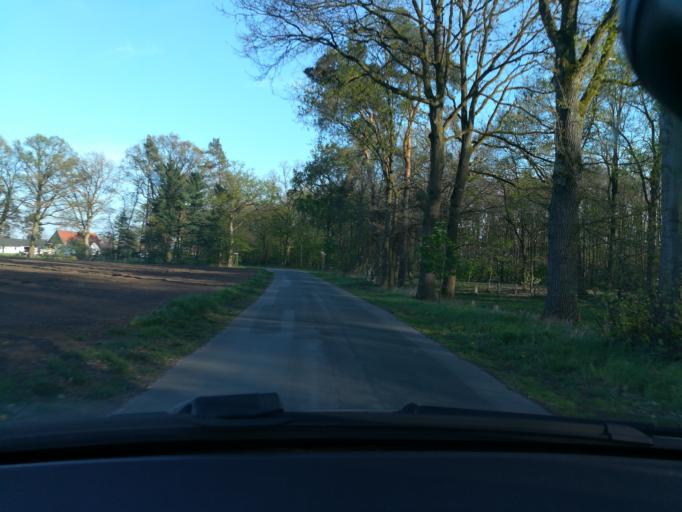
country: DE
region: North Rhine-Westphalia
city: Versmold
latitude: 52.0166
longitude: 8.1043
